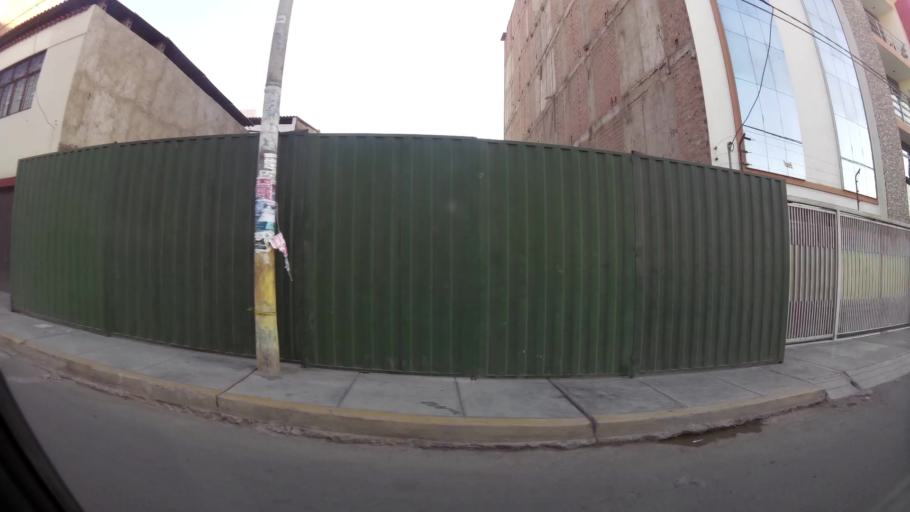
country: PE
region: Lambayeque
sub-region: Provincia de Chiclayo
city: Chiclayo
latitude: -6.7680
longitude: -79.8473
